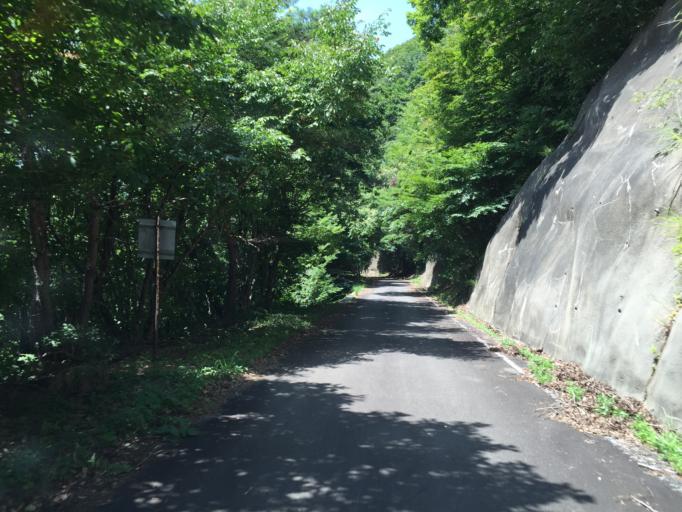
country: JP
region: Fukushima
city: Inawashiro
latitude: 37.4462
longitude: 140.0560
